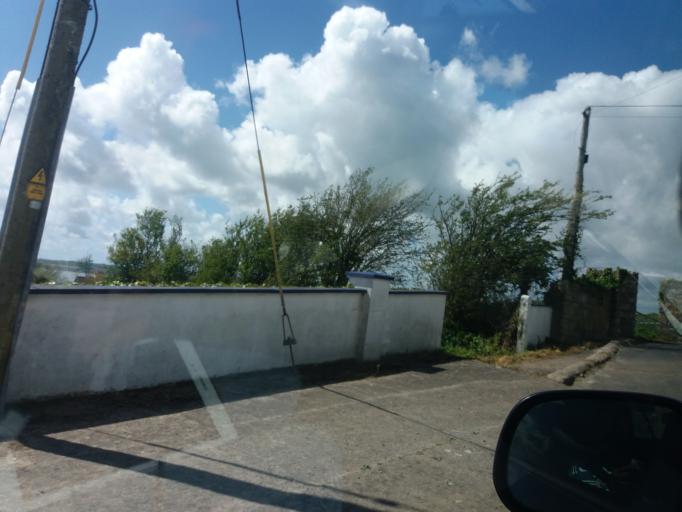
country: IE
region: Munster
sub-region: Waterford
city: Dunmore East
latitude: 52.2226
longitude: -6.9319
